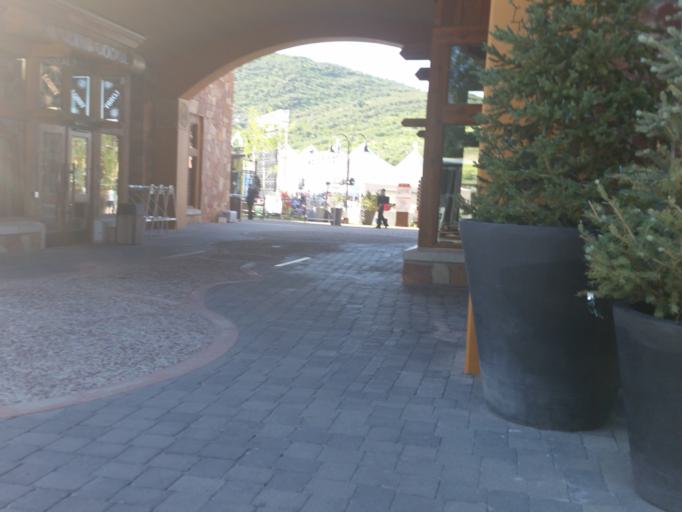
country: US
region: Utah
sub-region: Summit County
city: Snyderville
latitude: 40.6844
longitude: -111.5566
